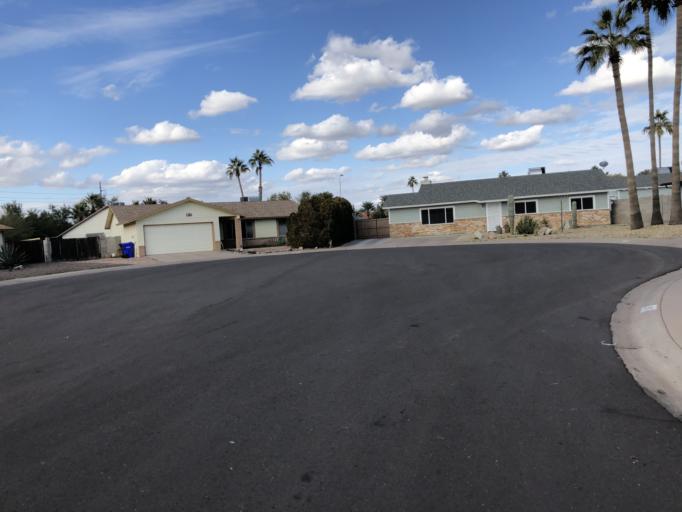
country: US
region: Arizona
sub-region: Maricopa County
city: San Carlos
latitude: 33.3121
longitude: -111.9104
